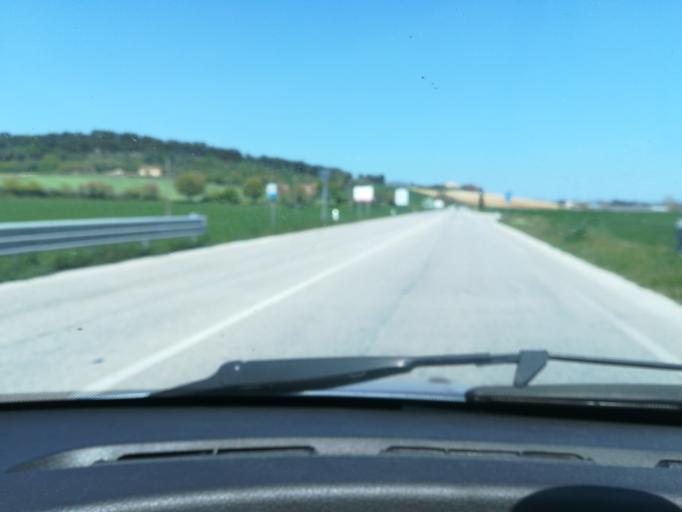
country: IT
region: The Marches
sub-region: Provincia di Ancona
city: Villa Musone
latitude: 43.4577
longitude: 13.5967
